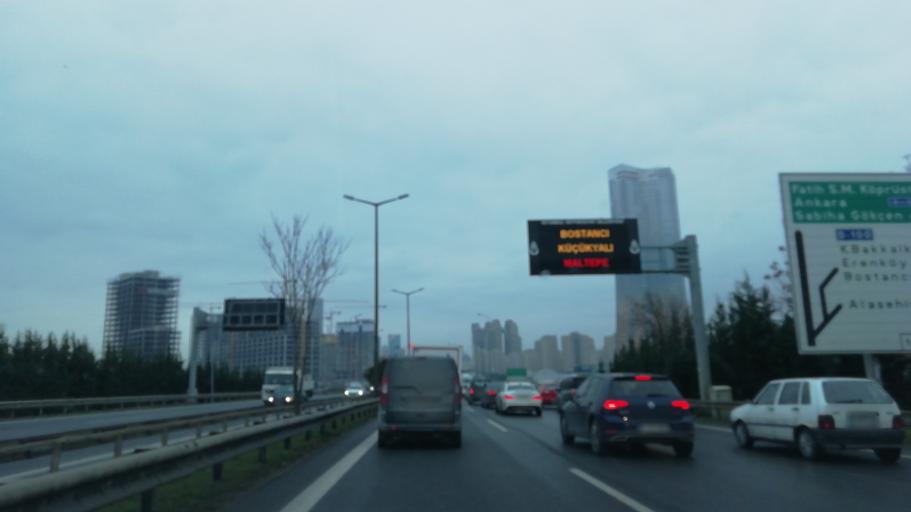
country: TR
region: Istanbul
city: Umraniye
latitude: 41.0056
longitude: 29.0997
